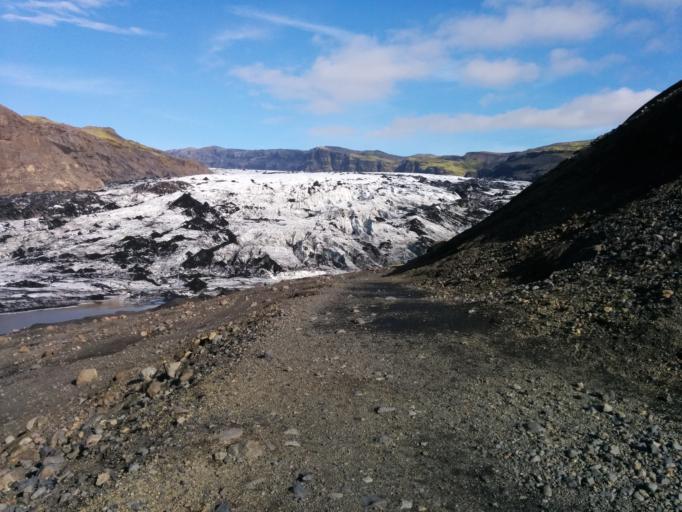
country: IS
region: South
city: Vestmannaeyjar
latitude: 63.5338
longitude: -19.3602
